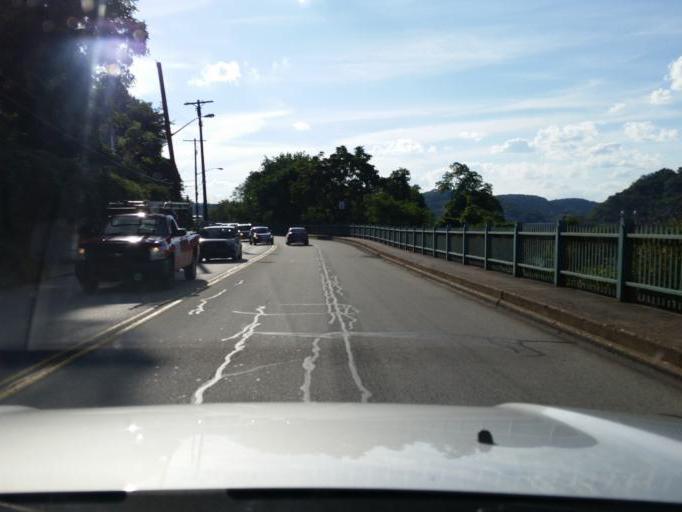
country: US
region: Pennsylvania
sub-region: Allegheny County
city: Sharpsburg
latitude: 40.4893
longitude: -79.9264
